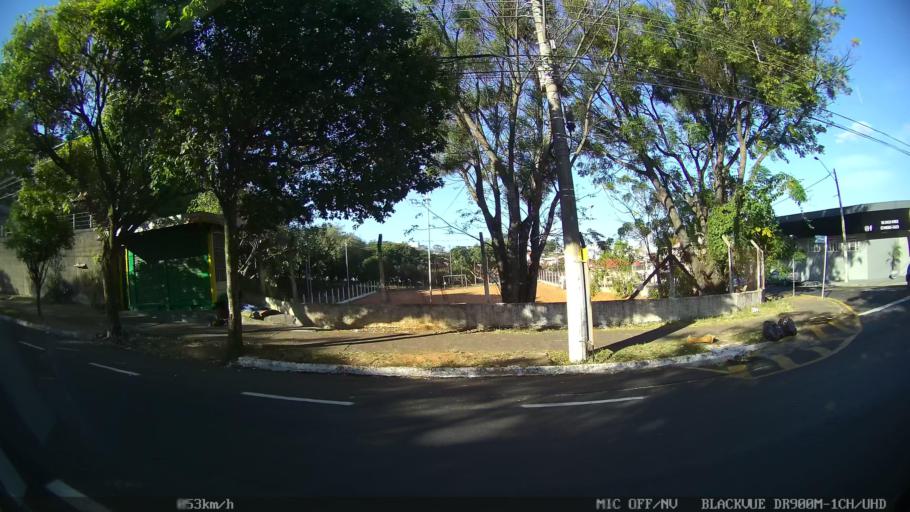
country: BR
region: Sao Paulo
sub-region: Franca
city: Franca
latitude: -20.5119
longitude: -47.3994
